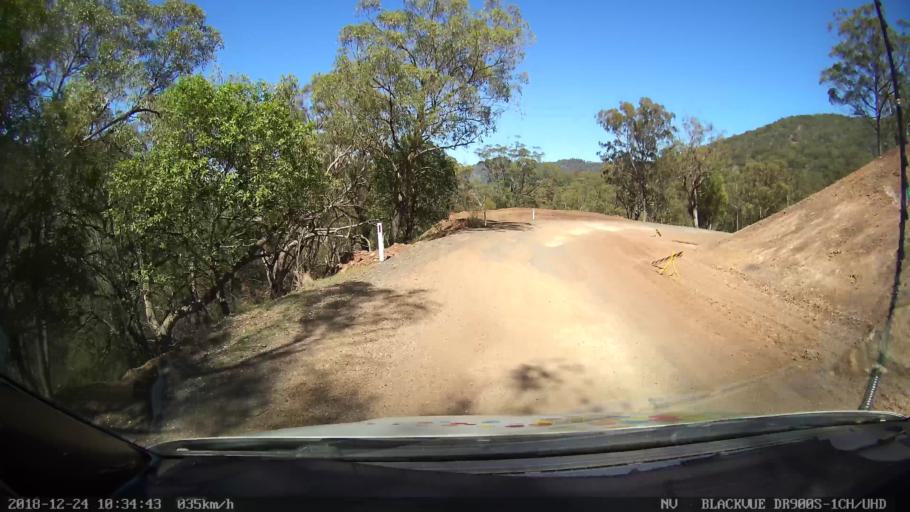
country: AU
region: New South Wales
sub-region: Upper Hunter Shire
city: Merriwa
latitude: -31.8419
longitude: 150.5045
